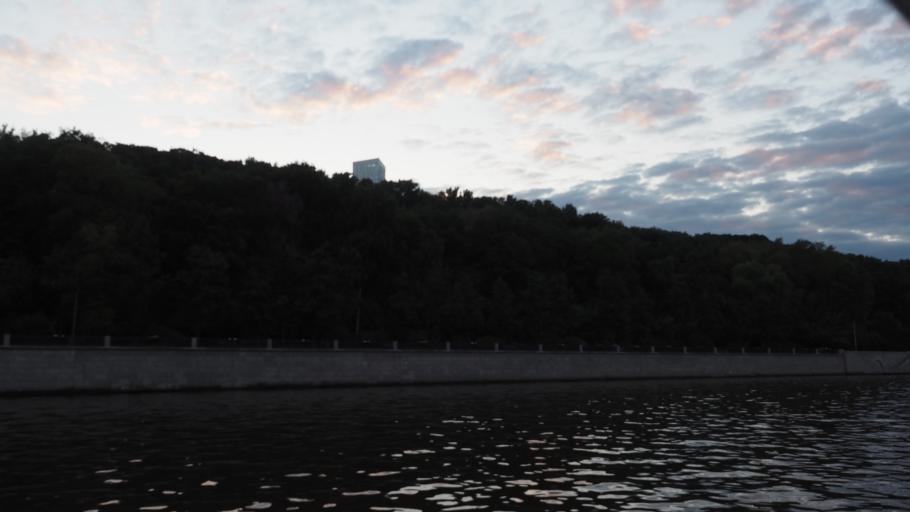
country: RU
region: Moscow
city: Vorob'yovo
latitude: 55.7188
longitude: 37.5410
